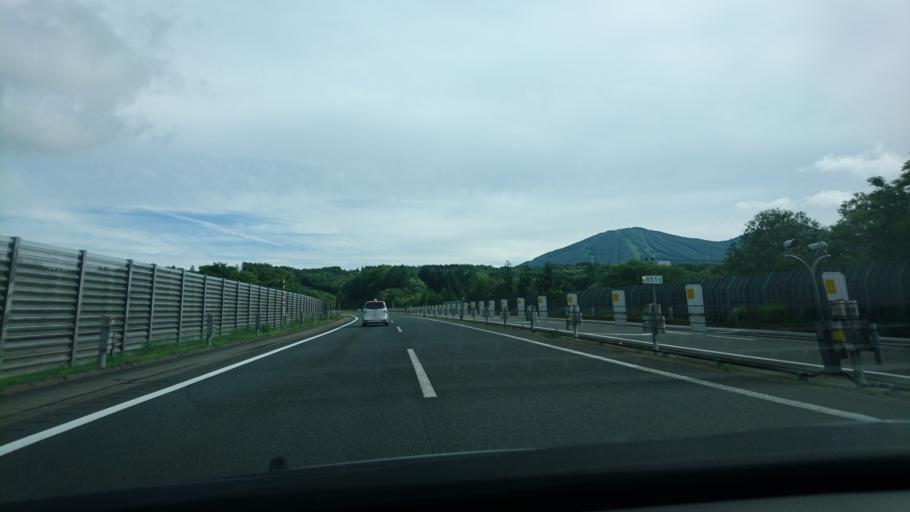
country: JP
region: Akita
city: Hanawa
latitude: 40.0257
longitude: 140.9828
